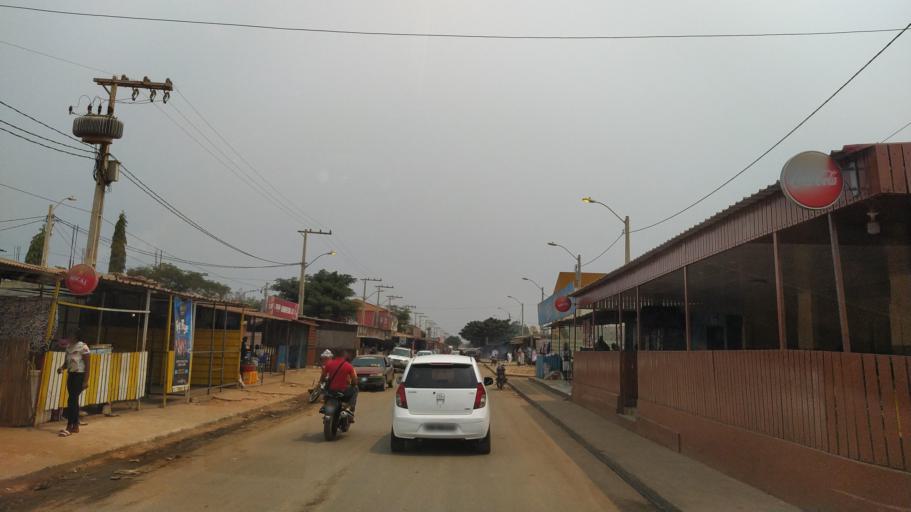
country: AO
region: Luanda
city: Luanda
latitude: -9.0722
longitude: 13.4075
